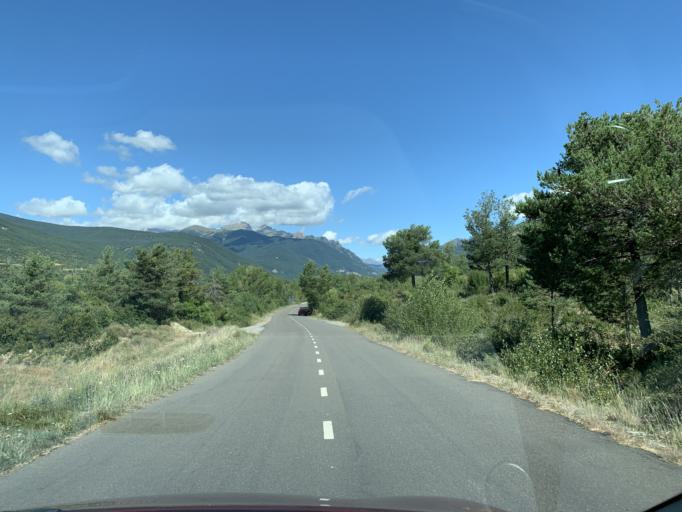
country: ES
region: Aragon
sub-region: Provincia de Huesca
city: Biescas
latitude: 42.5633
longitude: -0.3130
